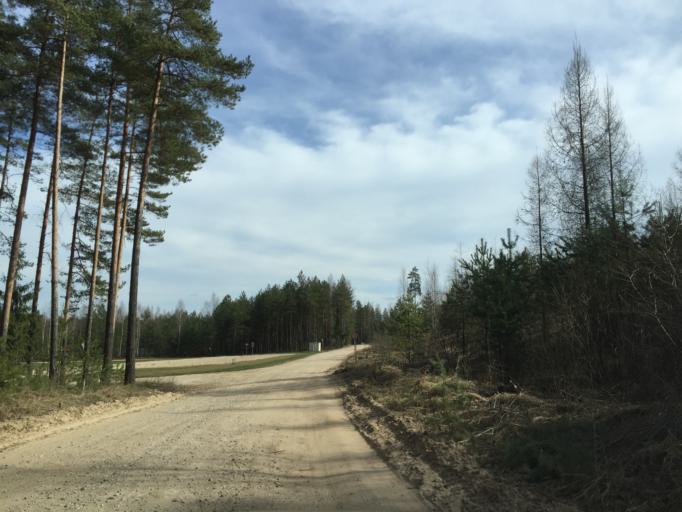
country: LV
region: Ogre
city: Ogre
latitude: 56.8418
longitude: 24.5662
